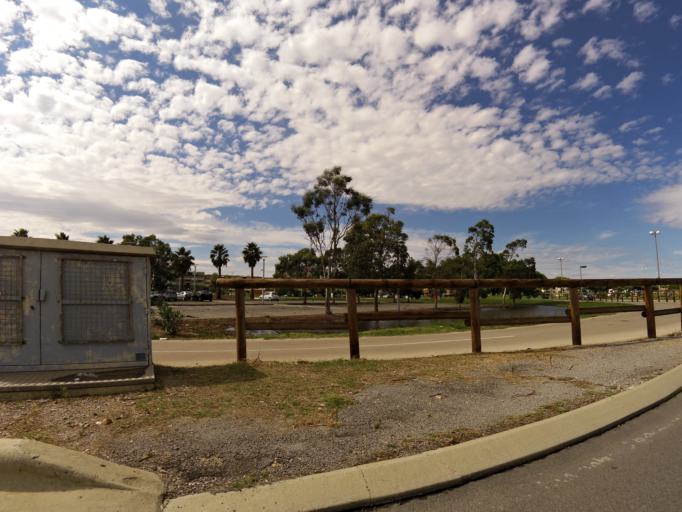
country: FR
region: Languedoc-Roussillon
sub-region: Departement du Gard
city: Le Grau-du-Roi
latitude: 43.5252
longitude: 4.1503
